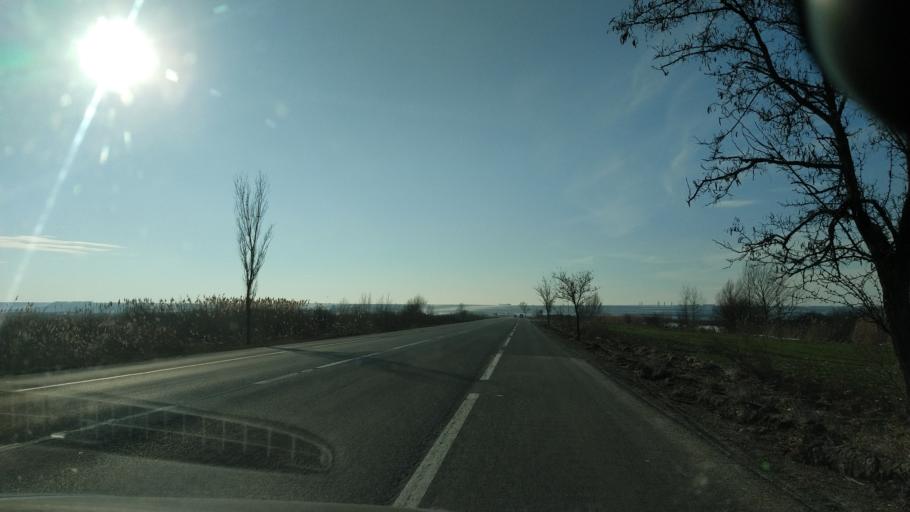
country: RO
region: Iasi
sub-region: Comuna Butea
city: Butea
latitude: 47.0715
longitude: 26.8873
